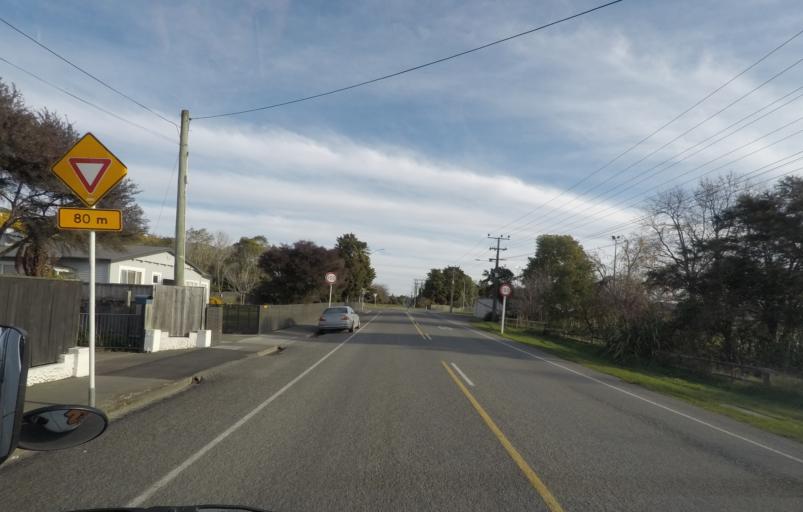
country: NZ
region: Tasman
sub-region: Tasman District
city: Brightwater
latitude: -41.3770
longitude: 173.1026
